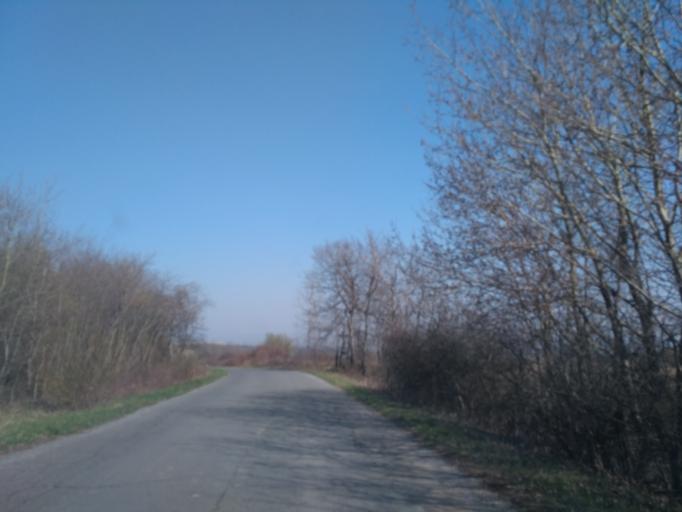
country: SK
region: Presovsky
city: Vranov nad Topl'ou
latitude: 48.8151
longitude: 21.6379
